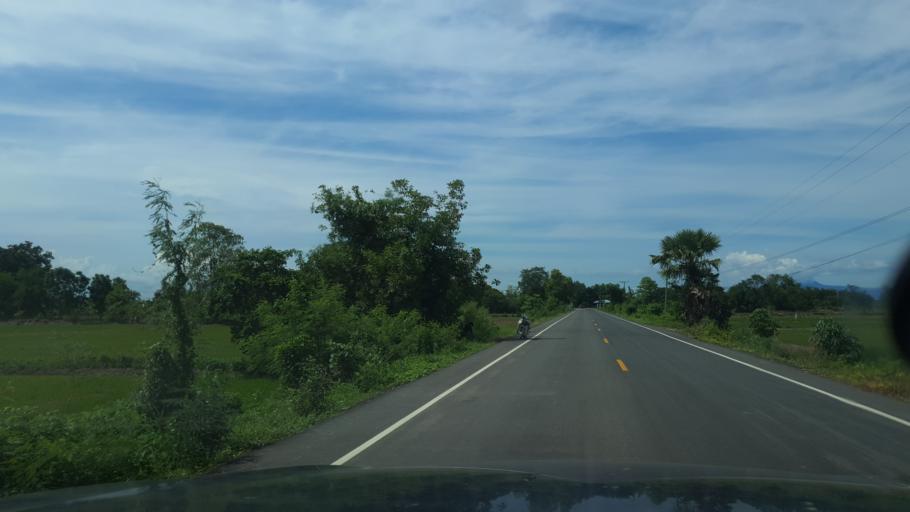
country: TH
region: Sukhothai
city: Si Samrong
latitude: 17.1778
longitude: 99.7372
